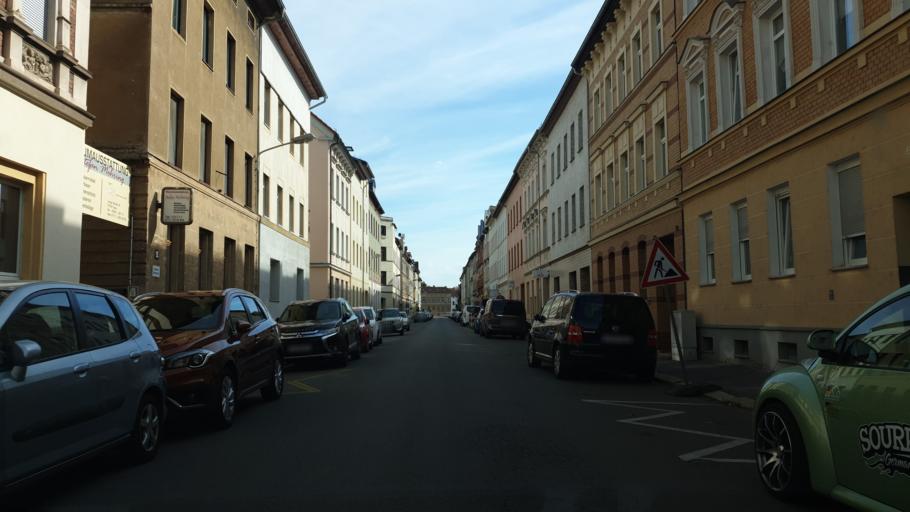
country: DE
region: Thuringia
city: Gera
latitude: 50.8522
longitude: 12.0846
